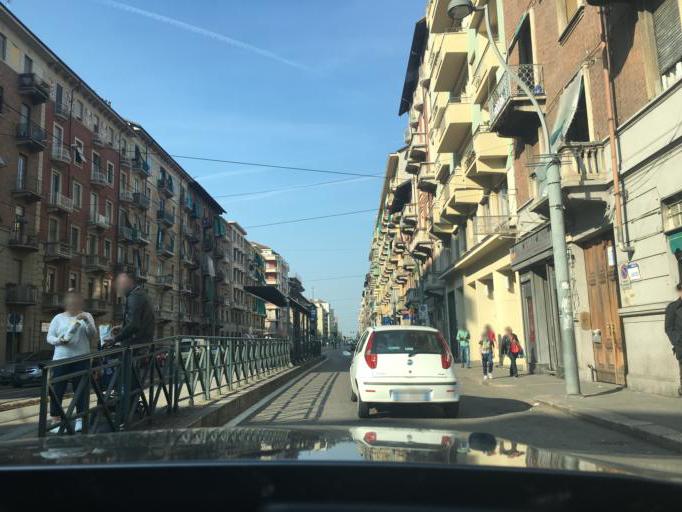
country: IT
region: Piedmont
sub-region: Provincia di Torino
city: Turin
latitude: 45.0945
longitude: 7.6953
